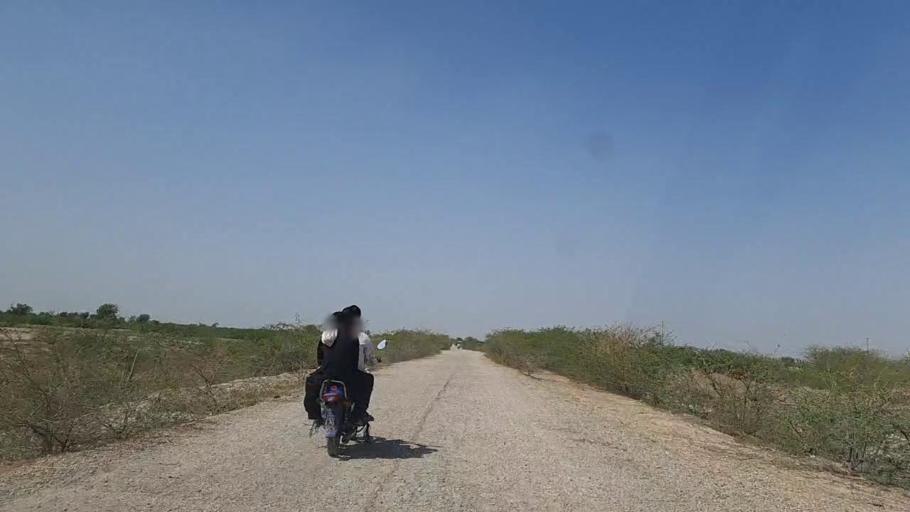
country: PK
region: Sindh
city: Naukot
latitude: 24.6203
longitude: 69.2916
